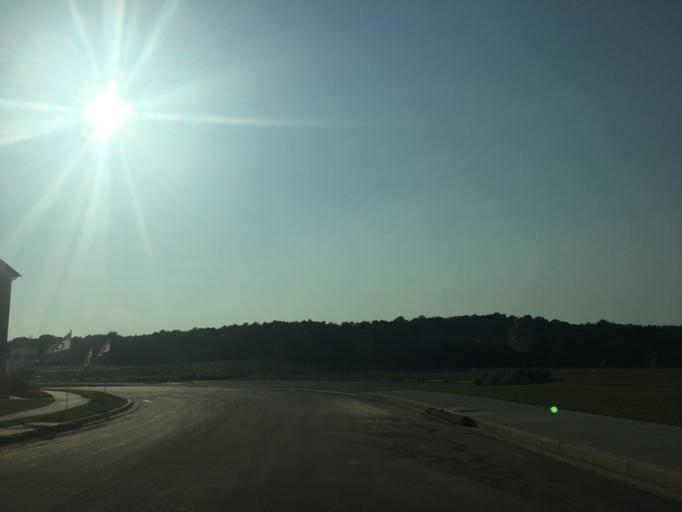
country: US
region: Maryland
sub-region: Frederick County
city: Green Valley
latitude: 39.3597
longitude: -77.2842
